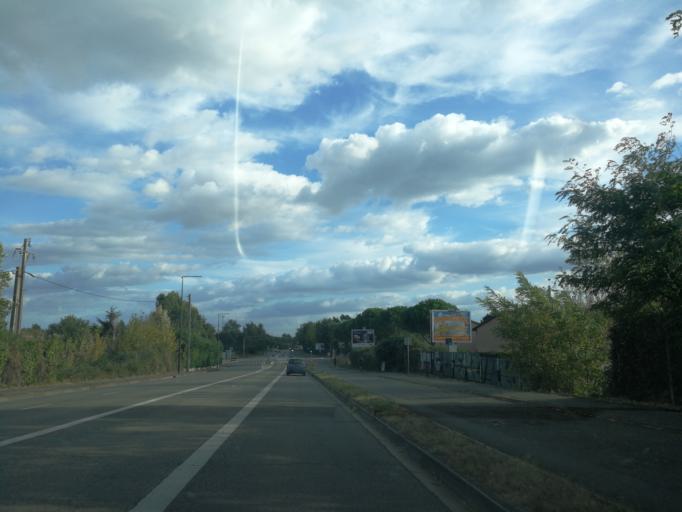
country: FR
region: Midi-Pyrenees
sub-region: Departement de la Haute-Garonne
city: L'Union
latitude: 43.6325
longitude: 1.4746
